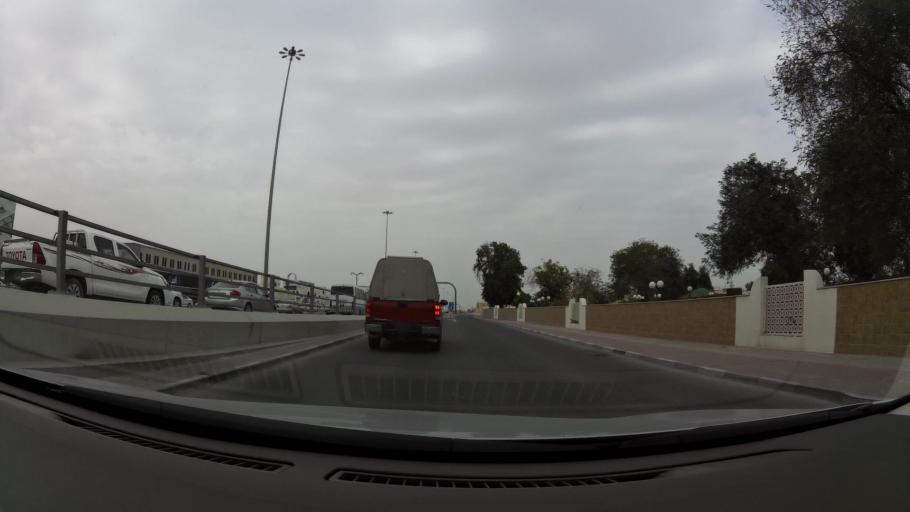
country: QA
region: Baladiyat ar Rayyan
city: Ar Rayyan
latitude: 25.3240
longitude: 51.4686
